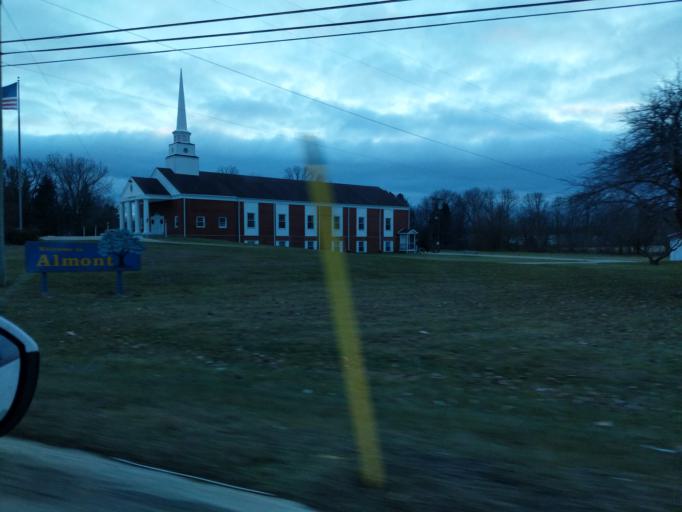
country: US
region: Michigan
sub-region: Lapeer County
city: Almont
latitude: 42.9292
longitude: -83.0510
